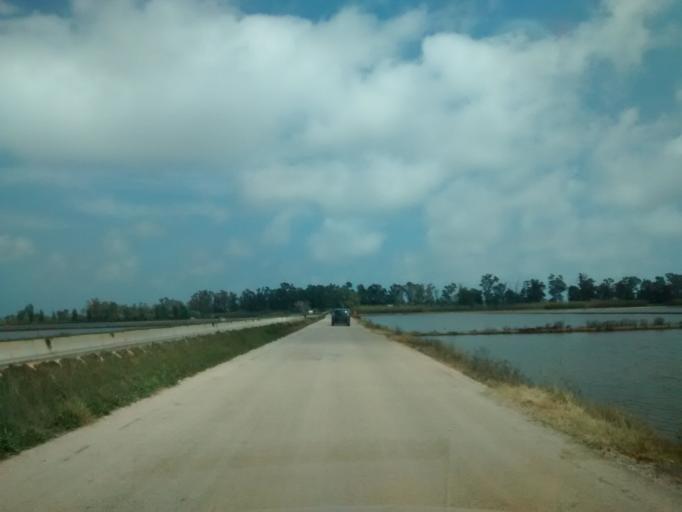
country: ES
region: Catalonia
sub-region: Provincia de Tarragona
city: Deltebre
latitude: 40.7024
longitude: 0.8205
